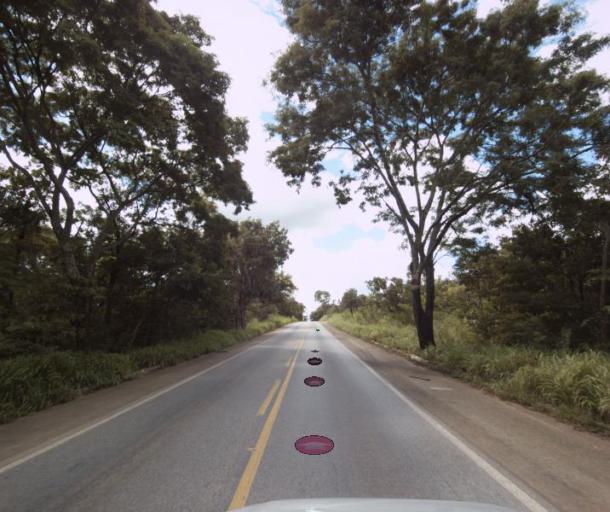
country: BR
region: Goias
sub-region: Porangatu
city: Porangatu
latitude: -13.8180
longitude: -49.0407
